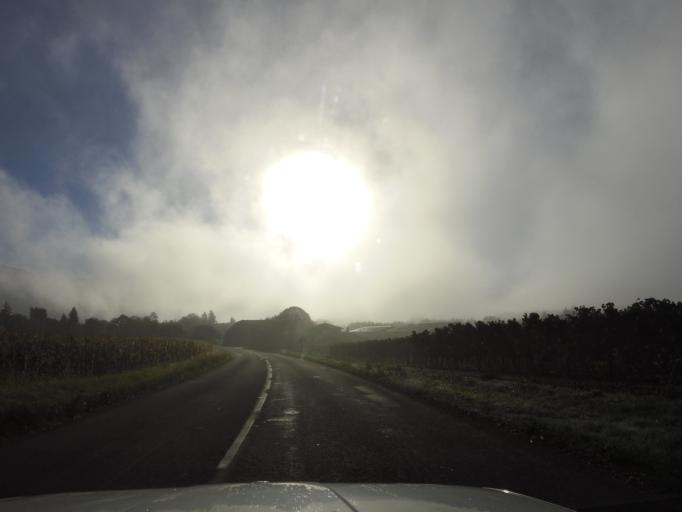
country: FR
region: Rhone-Alpes
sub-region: Departement de l'Ain
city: Lagnieu
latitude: 45.8857
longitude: 5.3410
